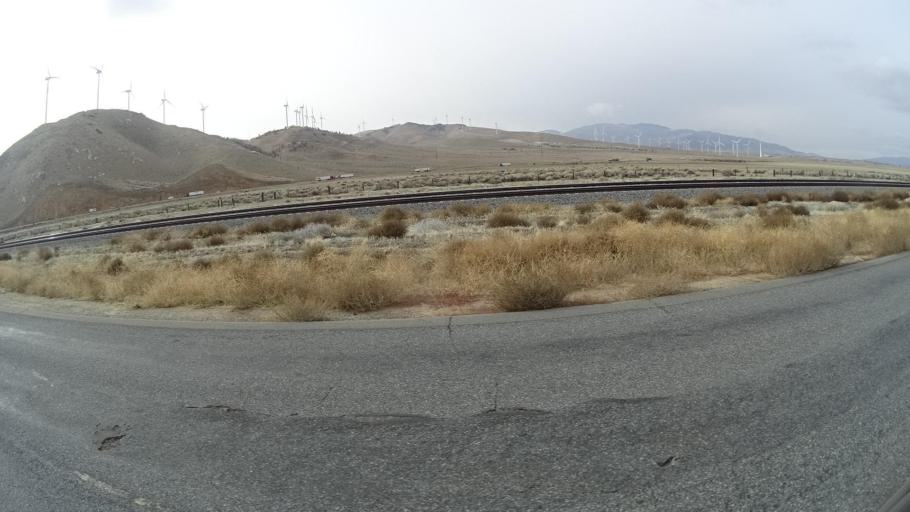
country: US
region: California
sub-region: Kern County
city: Tehachapi
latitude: 35.1148
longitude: -118.3325
